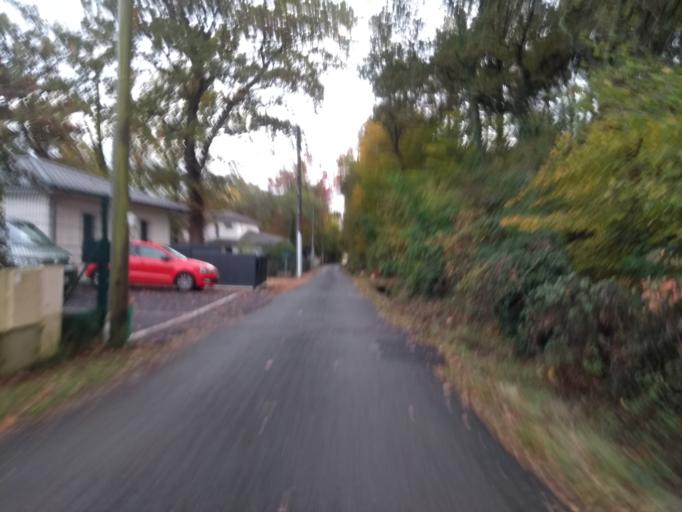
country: FR
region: Aquitaine
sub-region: Departement de la Gironde
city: Canejan
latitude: 44.7660
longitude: -0.6430
